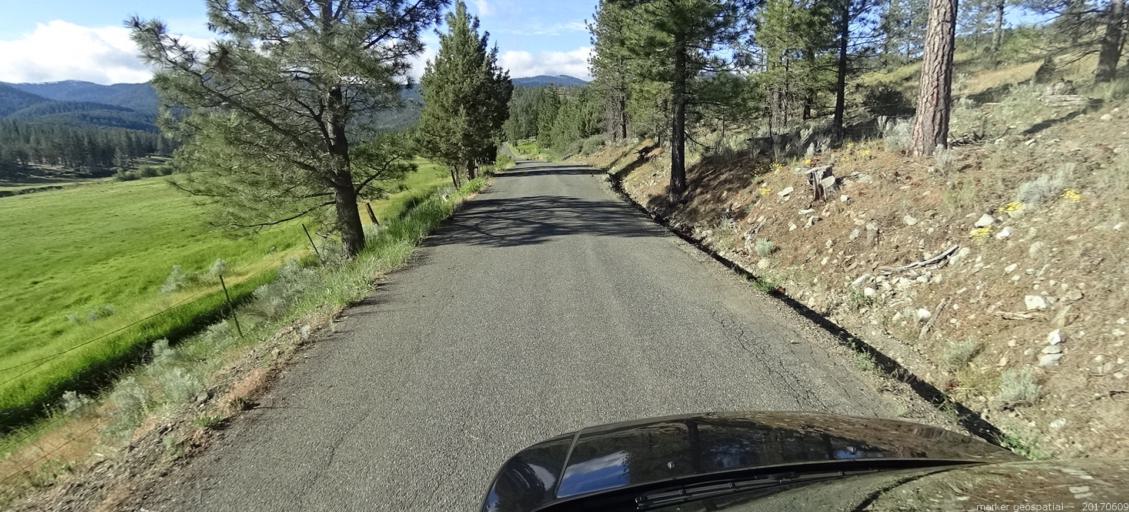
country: US
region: California
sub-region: Siskiyou County
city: Weed
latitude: 41.3469
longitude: -122.7237
